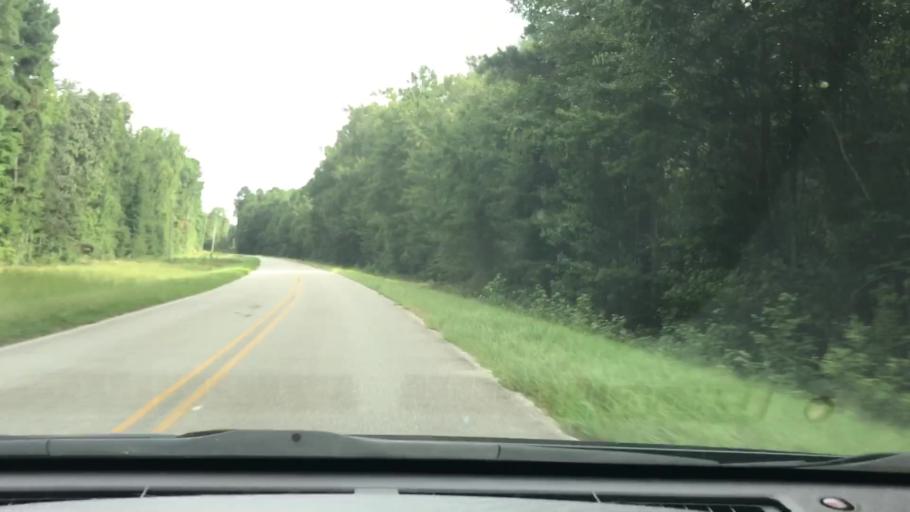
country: US
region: Georgia
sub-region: Jefferson County
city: Wadley
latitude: 32.8183
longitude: -82.3766
